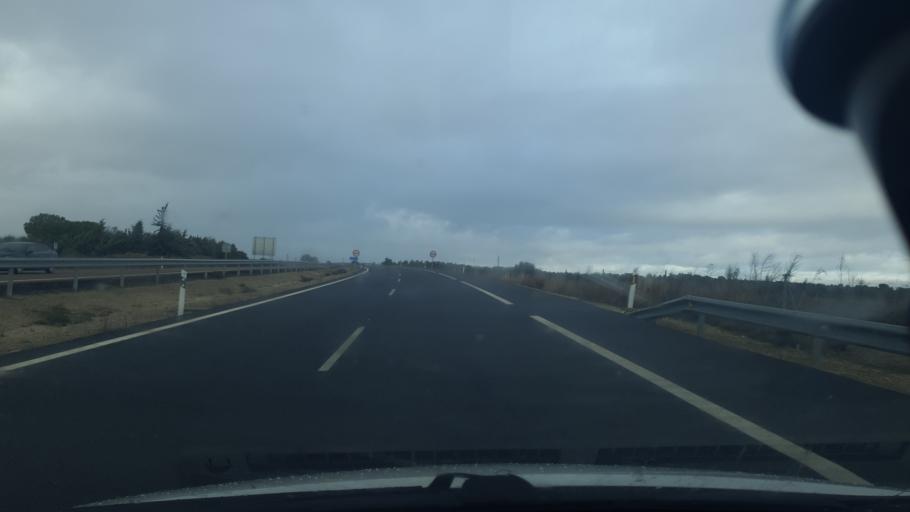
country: ES
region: Castille and Leon
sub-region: Provincia de Segovia
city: Cuellar
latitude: 41.4097
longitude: -4.2999
